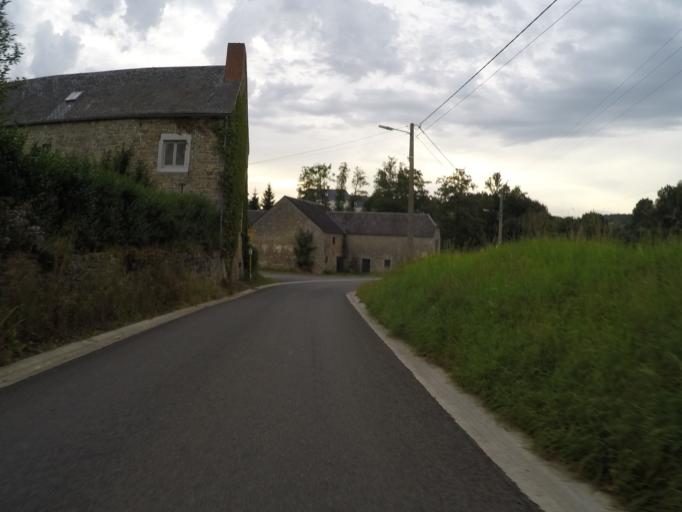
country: BE
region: Wallonia
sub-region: Province de Namur
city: Assesse
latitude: 50.3254
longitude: 5.0379
